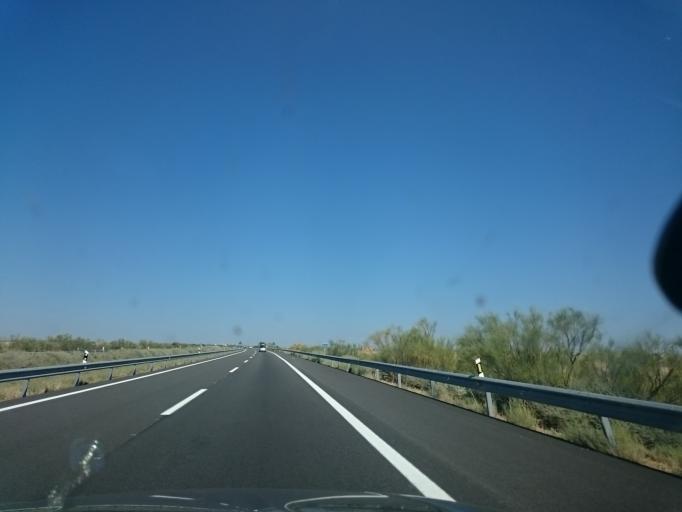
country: ES
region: Aragon
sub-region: Provincia de Zaragoza
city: Mequinensa / Mequinenza
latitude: 41.4674
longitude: 0.2367
